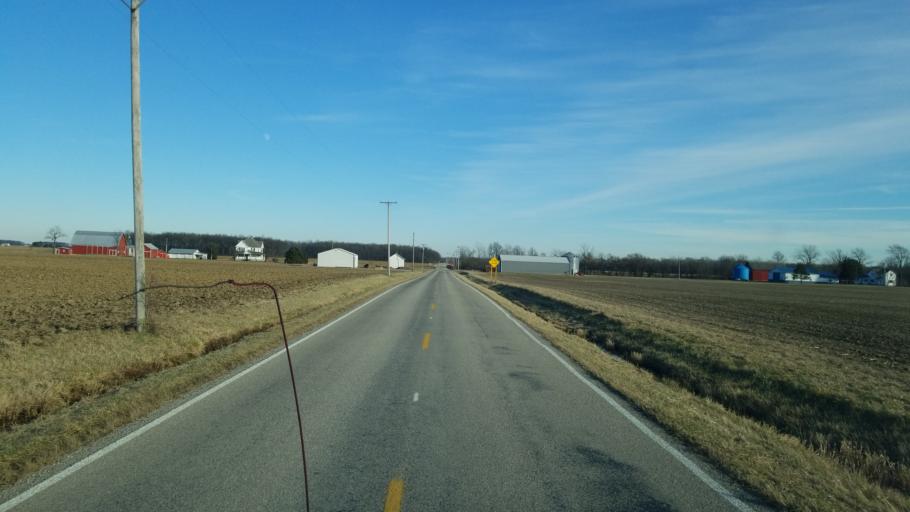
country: US
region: Ohio
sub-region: Huron County
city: Bellevue
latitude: 41.1796
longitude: -82.7911
